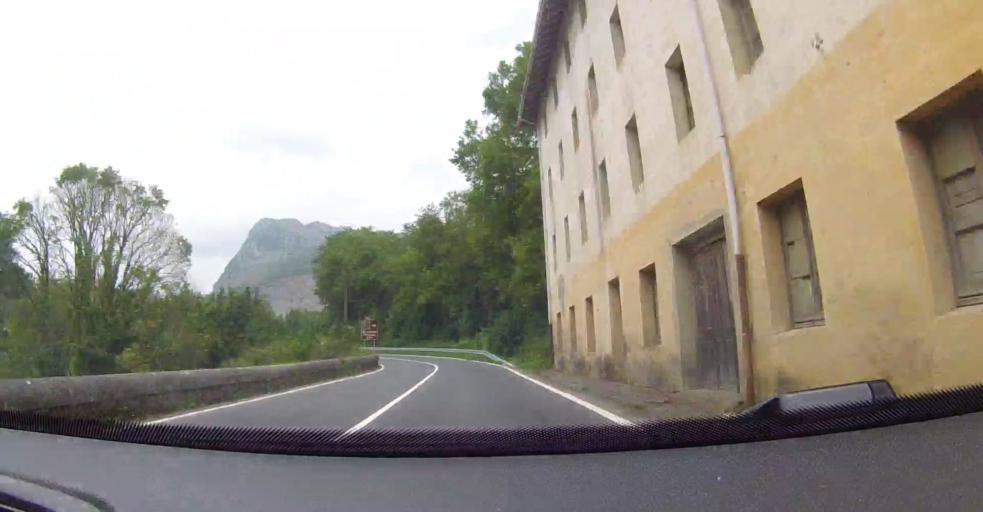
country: ES
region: Basque Country
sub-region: Bizkaia
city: Lanestosa
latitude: 43.2453
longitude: -3.3697
